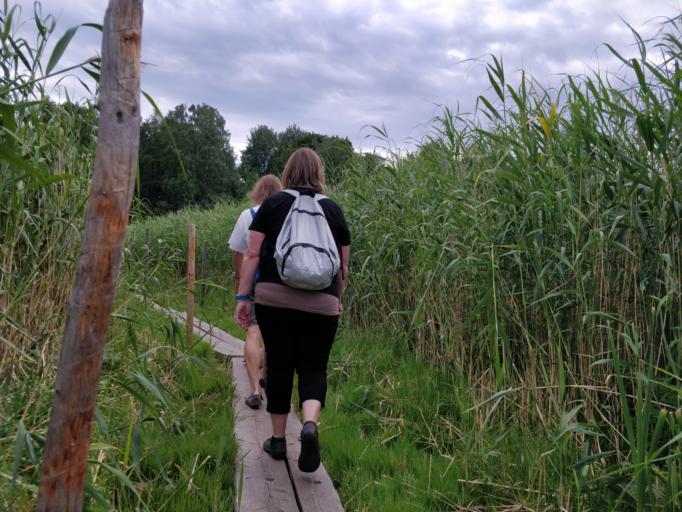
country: FI
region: Uusimaa
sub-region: Helsinki
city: Helsinki
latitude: 60.2055
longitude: 24.9956
